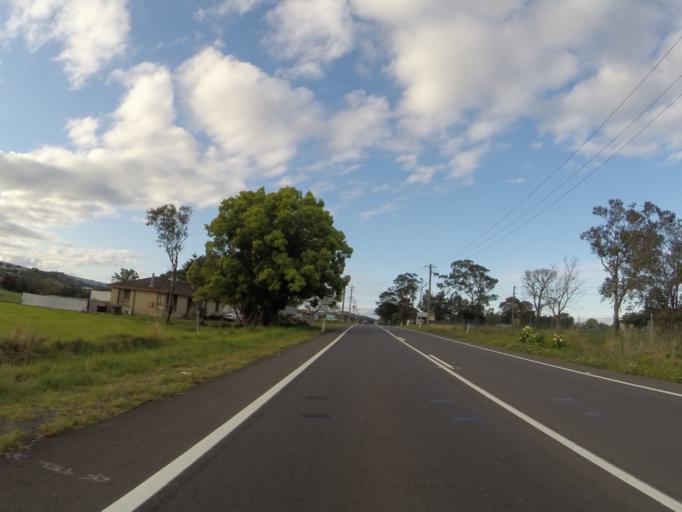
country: AU
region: New South Wales
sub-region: Shellharbour
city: Albion Park Rail
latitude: -34.5534
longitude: 150.7819
